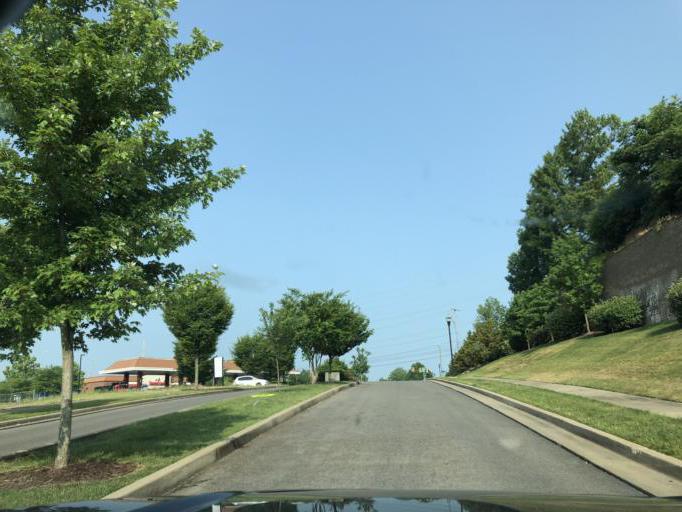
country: US
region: Tennessee
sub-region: Rutherford County
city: La Vergne
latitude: 36.0520
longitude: -86.6432
